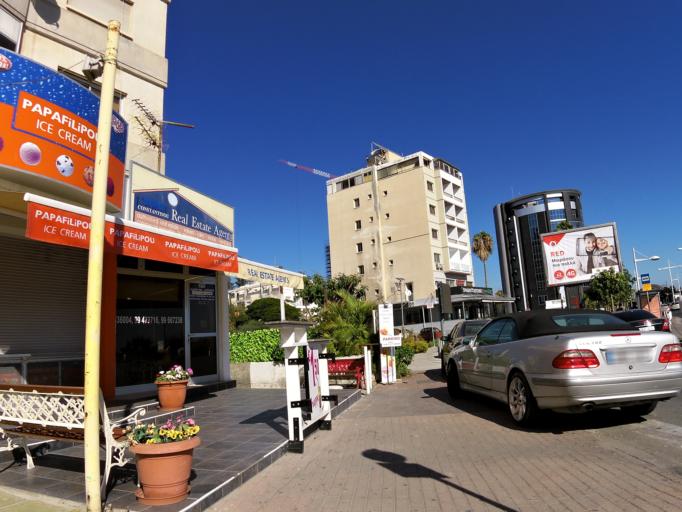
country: CY
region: Limassol
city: Limassol
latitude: 34.6885
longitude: 33.0686
